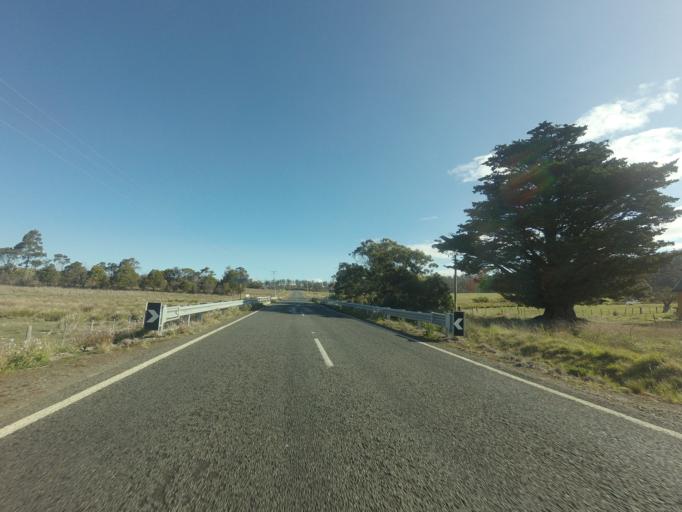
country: AU
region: Tasmania
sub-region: Sorell
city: Sorell
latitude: -42.4628
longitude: 147.9240
